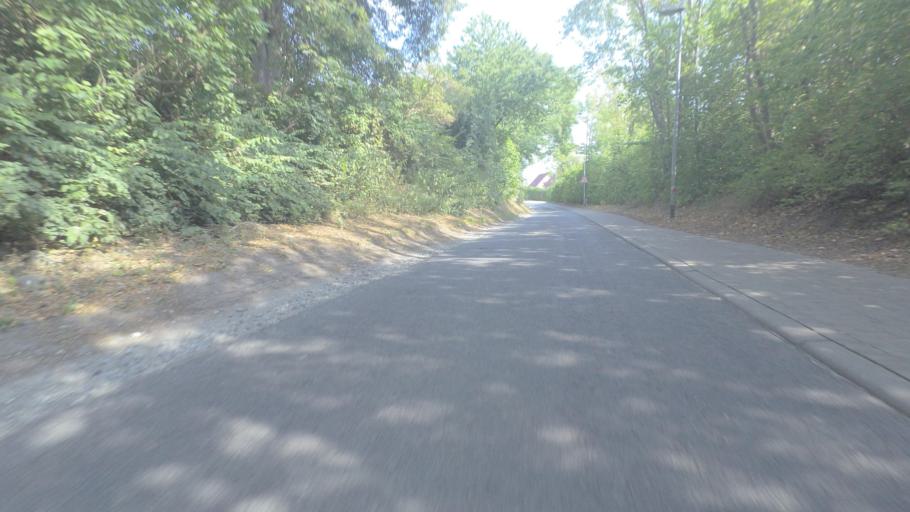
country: DE
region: Mecklenburg-Vorpommern
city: Wendorf
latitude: 54.2701
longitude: 13.0900
